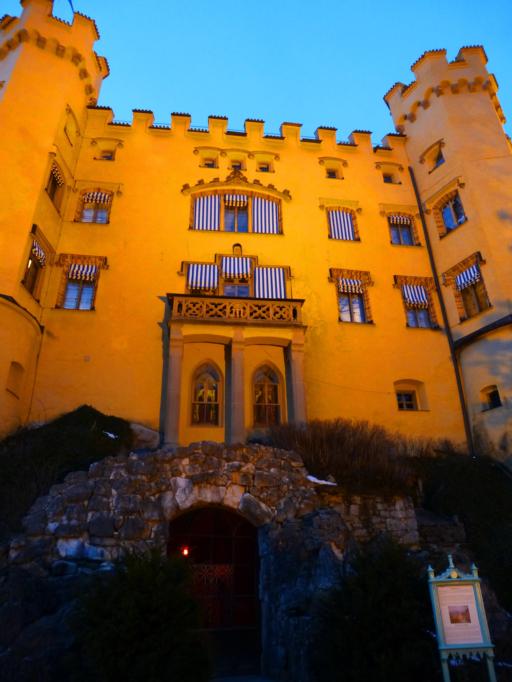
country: DE
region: Bavaria
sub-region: Swabia
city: Schwangau
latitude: 47.5555
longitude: 10.7366
